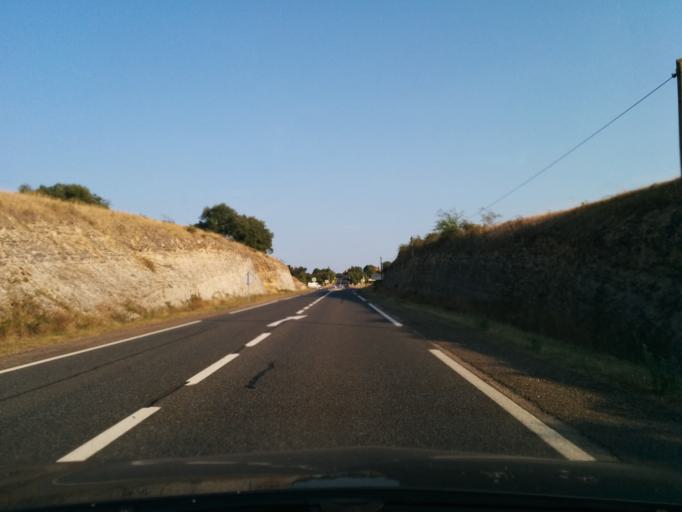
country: FR
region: Midi-Pyrenees
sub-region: Departement du Lot
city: Le Vigan
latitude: 44.6200
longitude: 1.4910
